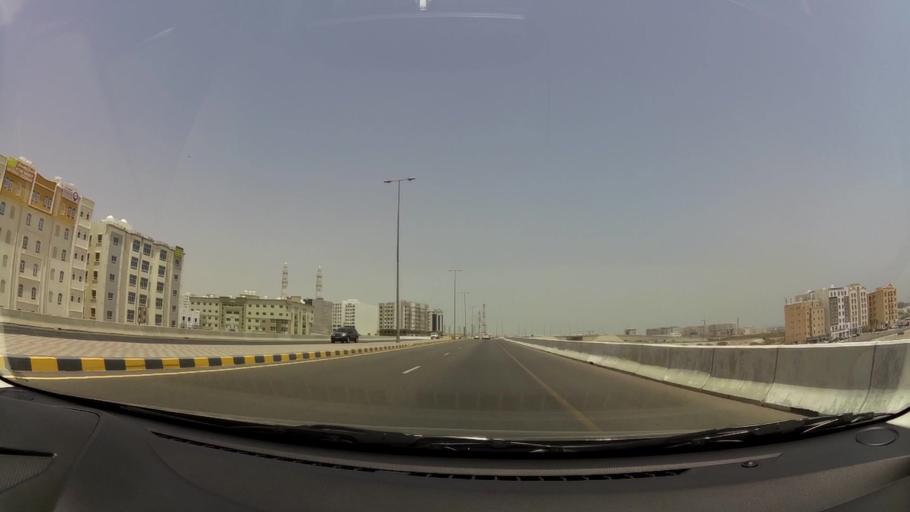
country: OM
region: Muhafazat Masqat
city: Bawshar
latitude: 23.5776
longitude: 58.4206
